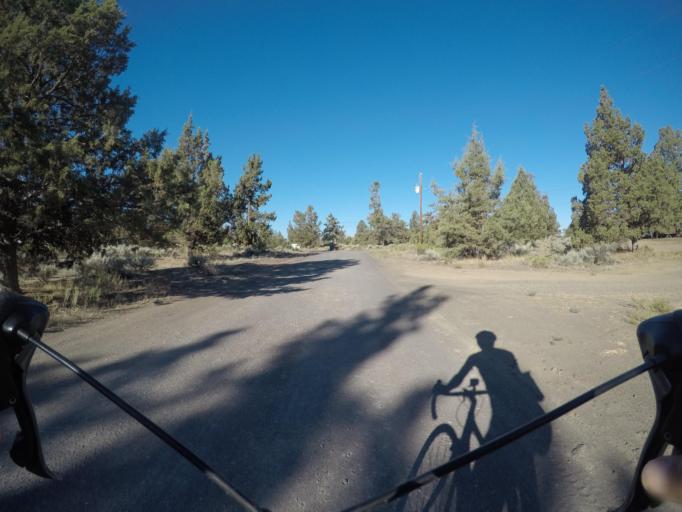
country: US
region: Oregon
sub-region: Deschutes County
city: Redmond
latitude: 44.2234
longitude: -121.2347
